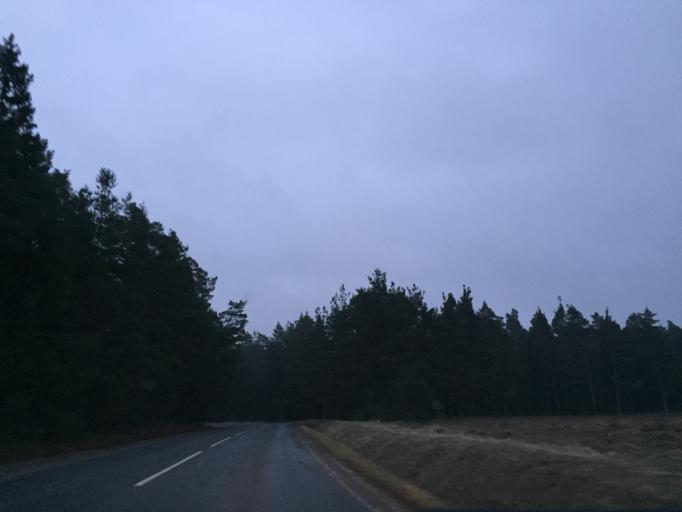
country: EE
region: Saare
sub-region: Kuressaare linn
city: Kuressaare
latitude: 58.5907
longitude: 22.6070
